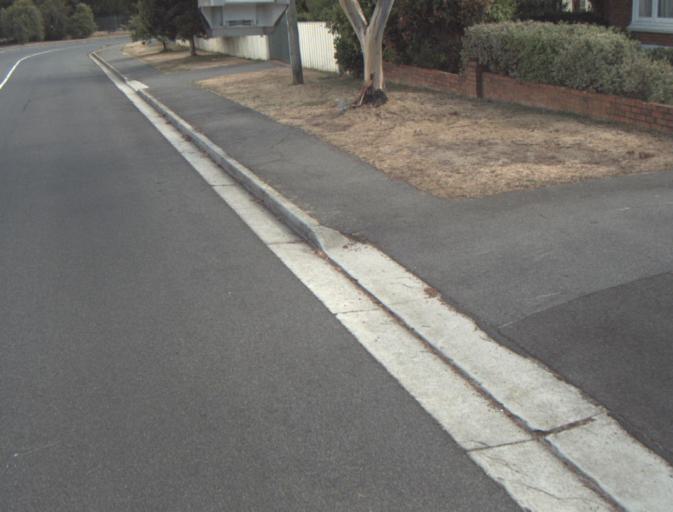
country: AU
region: Tasmania
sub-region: Launceston
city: Newstead
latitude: -41.4602
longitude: 147.1721
